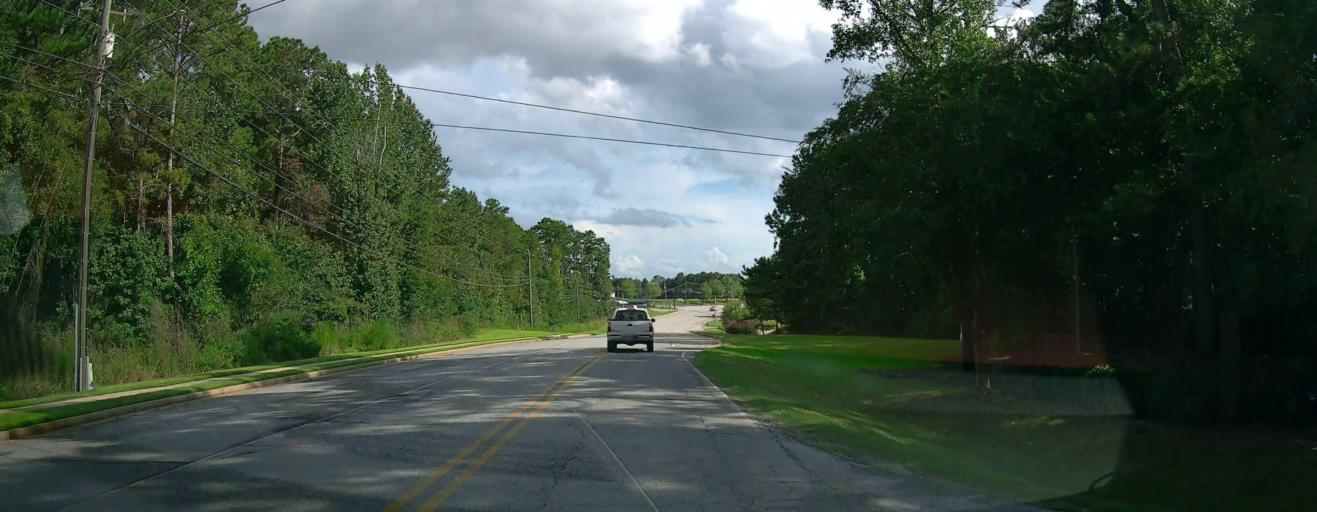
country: US
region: Alabama
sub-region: Russell County
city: Phenix City
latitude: 32.5738
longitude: -84.9698
